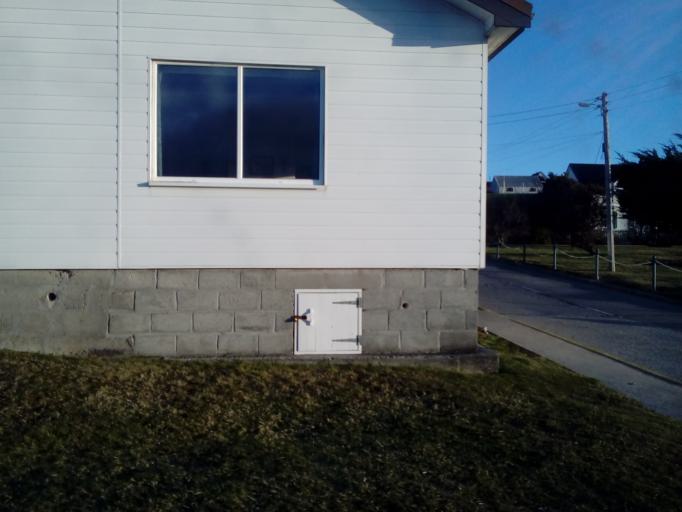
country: FK
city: Stanley
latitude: -51.6926
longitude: -57.8532
